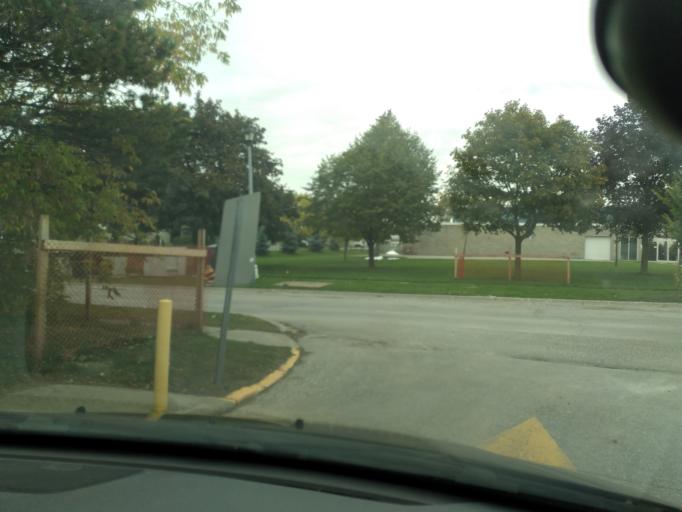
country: CA
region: Ontario
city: Newmarket
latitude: 44.0630
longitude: -79.4499
